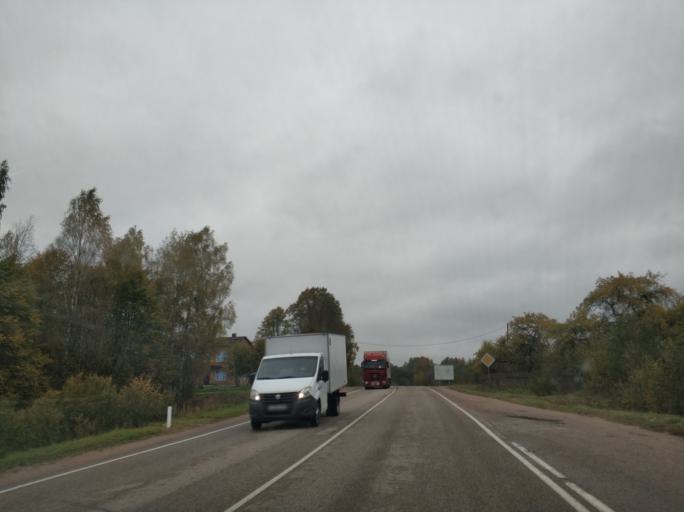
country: BY
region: Vitebsk
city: Rasony
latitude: 56.0566
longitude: 28.7134
